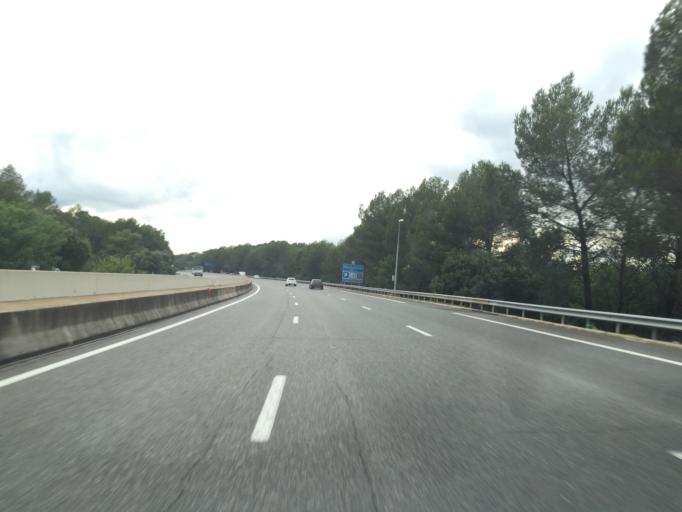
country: FR
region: Provence-Alpes-Cote d'Azur
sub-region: Departement du Var
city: Cabasse
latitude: 43.4055
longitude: 6.2081
